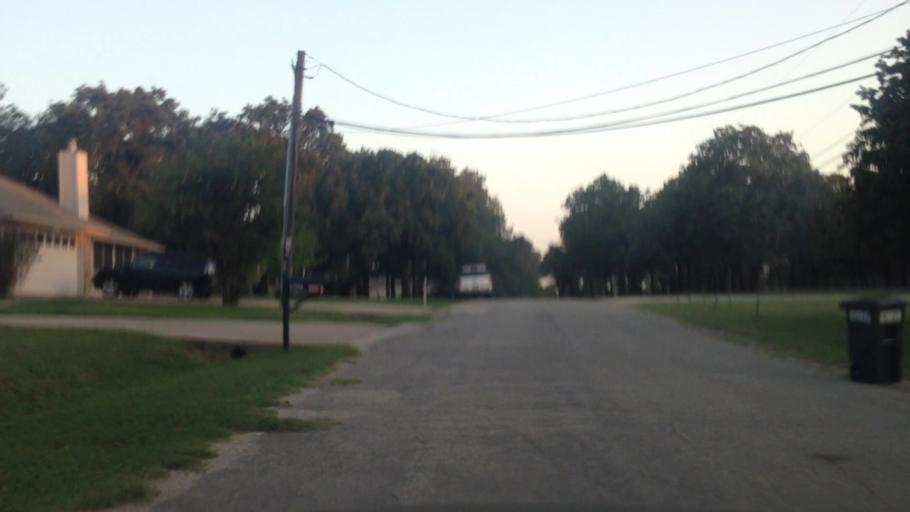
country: US
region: Texas
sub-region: Tarrant County
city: Kennedale
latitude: 32.6453
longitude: -97.2046
